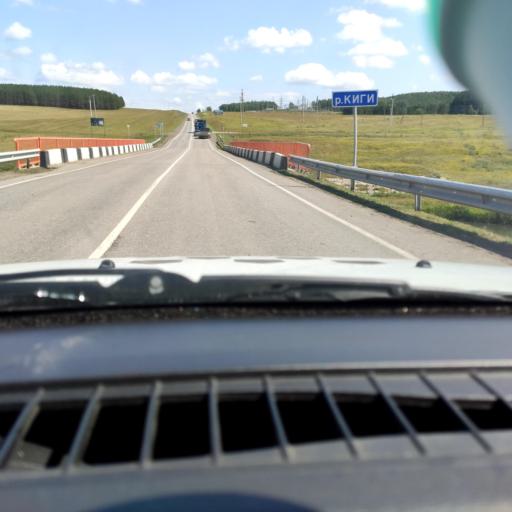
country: RU
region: Bashkortostan
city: Verkhniye Kigi
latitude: 55.3980
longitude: 58.6103
